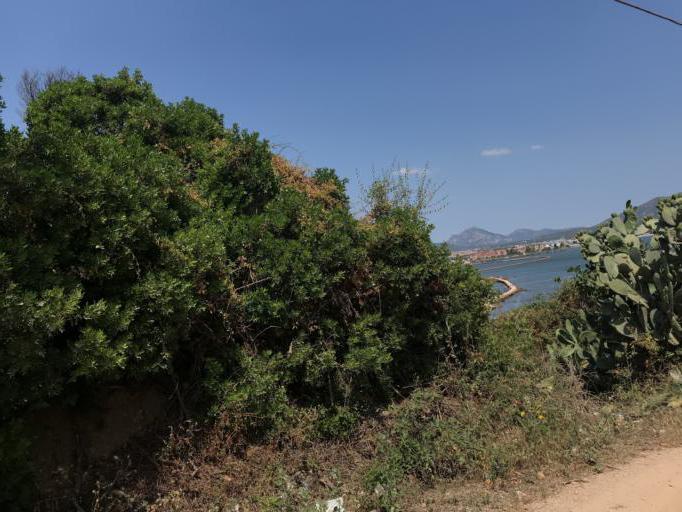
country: IT
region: Sardinia
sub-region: Provincia di Olbia-Tempio
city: Olbia
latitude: 40.9122
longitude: 9.5148
